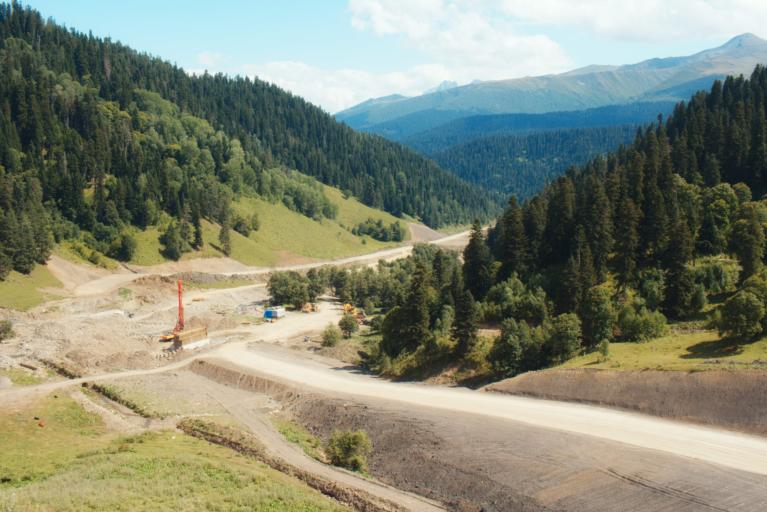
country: RU
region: Karachayevo-Cherkesiya
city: Mednogorskiy
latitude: 43.5771
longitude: 41.0996
